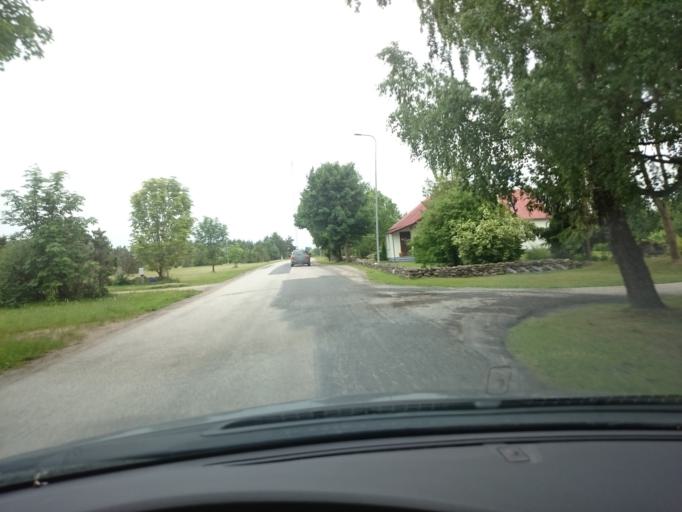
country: EE
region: Saare
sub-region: Orissaare vald
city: Orissaare
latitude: 58.6032
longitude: 23.2362
